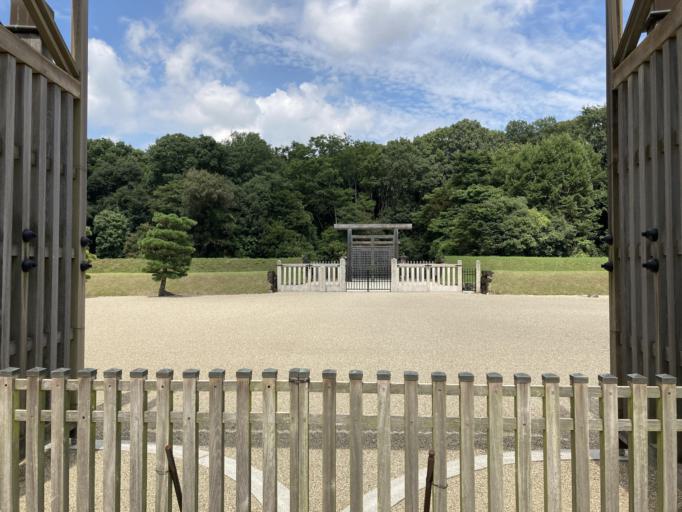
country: JP
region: Nara
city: Kashihara-shi
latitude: 34.4964
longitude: 135.7880
